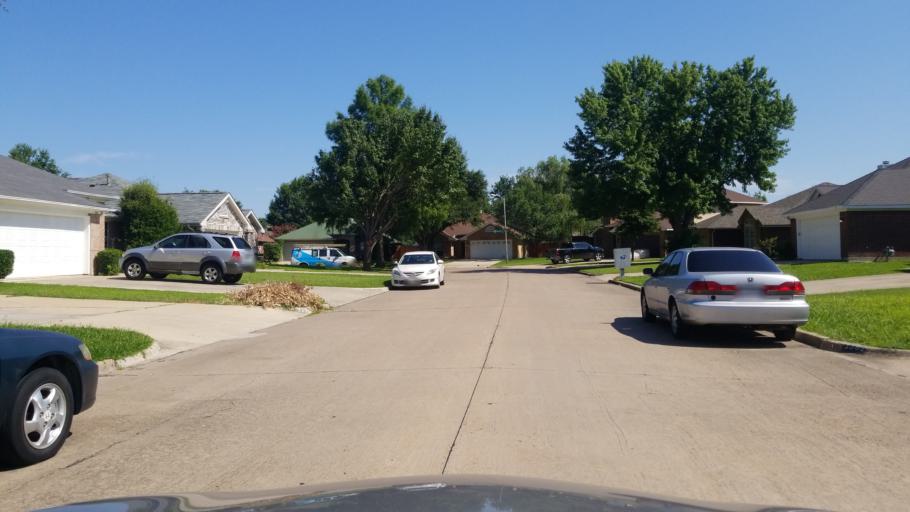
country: US
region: Texas
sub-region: Dallas County
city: Grand Prairie
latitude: 32.6903
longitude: -97.0141
